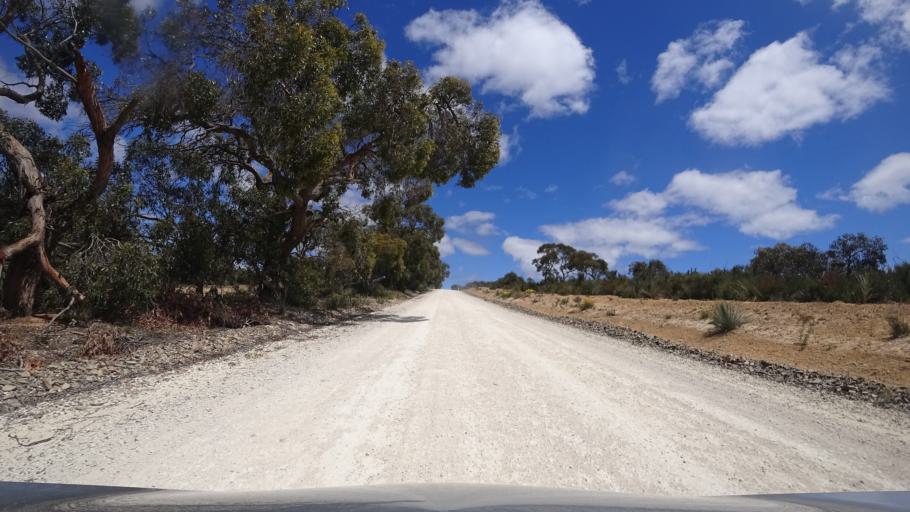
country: AU
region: South Australia
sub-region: Kangaroo Island
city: Kingscote
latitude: -35.6476
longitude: 137.3803
